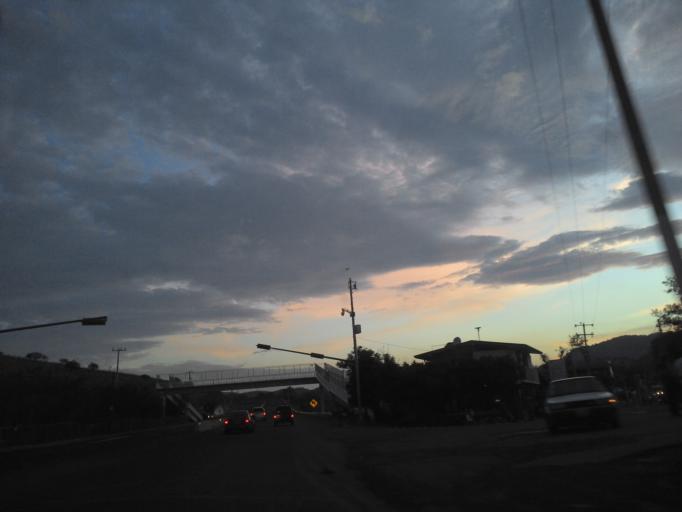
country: MX
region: Jalisco
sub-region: Zapopan
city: San Isidro
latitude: 20.7910
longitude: -103.3501
